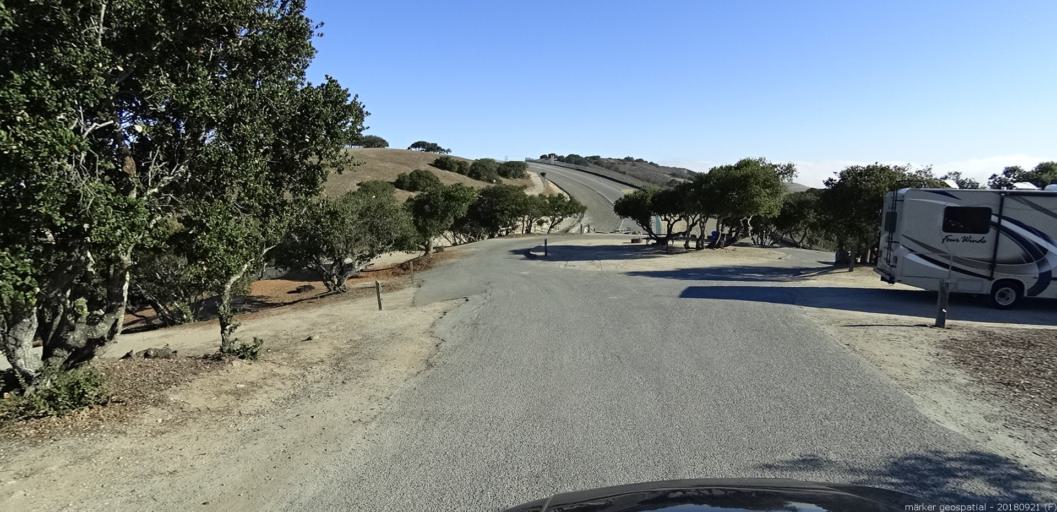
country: US
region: California
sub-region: Monterey County
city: Carmel Valley Village
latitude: 36.5796
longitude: -121.7503
